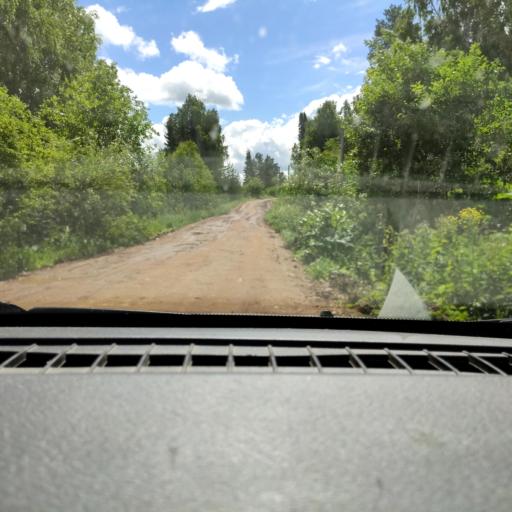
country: RU
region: Perm
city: Overyata
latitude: 58.1358
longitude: 55.8244
